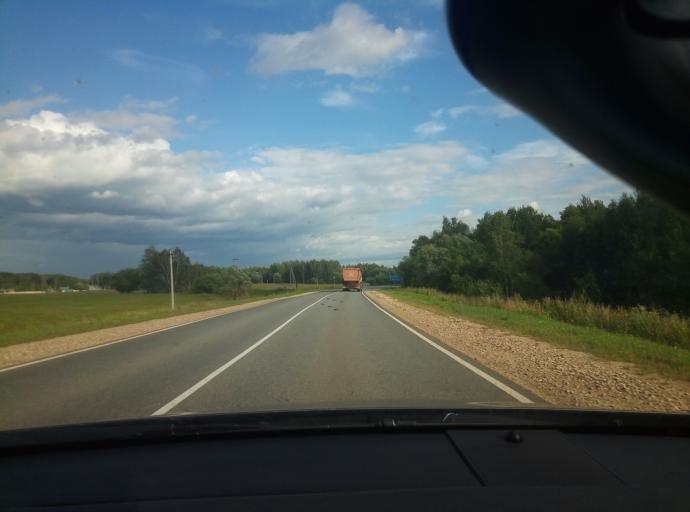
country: RU
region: Kaluga
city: Nikola-Lenivets
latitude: 54.5809
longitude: 35.4405
